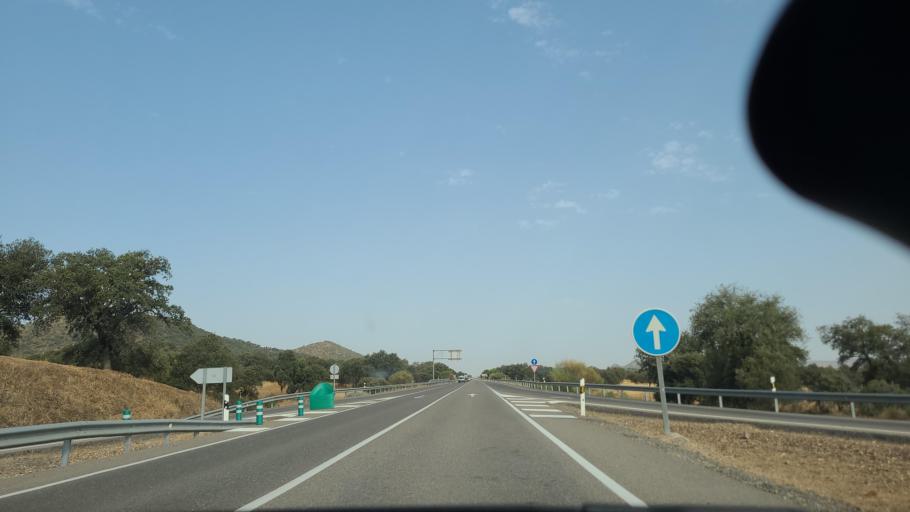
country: ES
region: Andalusia
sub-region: Province of Cordoba
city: Belmez
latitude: 38.2148
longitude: -5.1425
